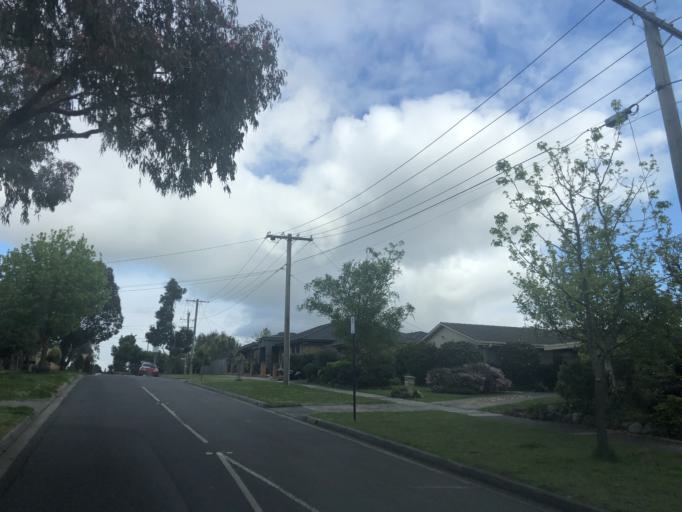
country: AU
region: Victoria
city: Burwood East
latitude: -37.8676
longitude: 145.1404
